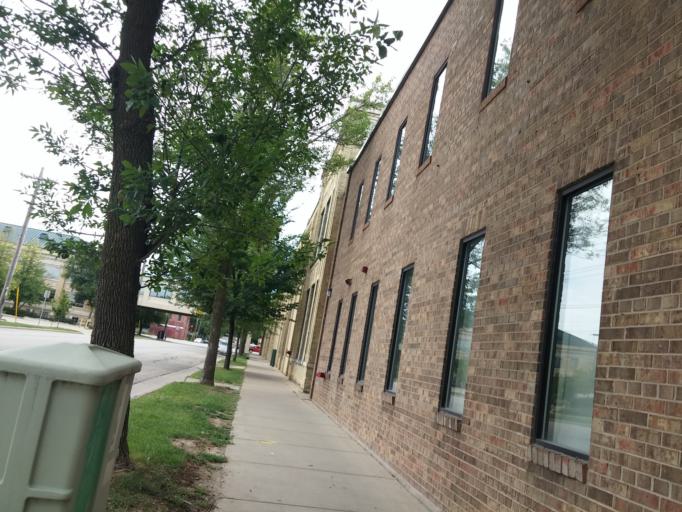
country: US
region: Wisconsin
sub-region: Dane County
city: Maple Bluff
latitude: 43.0865
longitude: -89.3650
